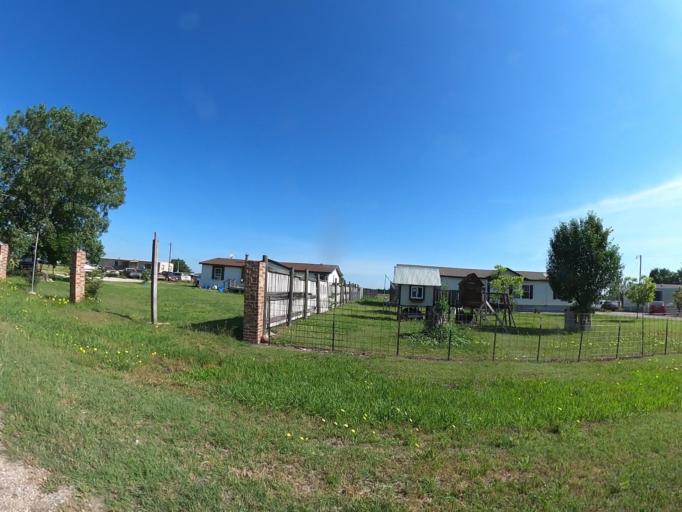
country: US
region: Texas
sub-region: Ellis County
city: Red Oak
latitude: 32.4420
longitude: -96.7739
